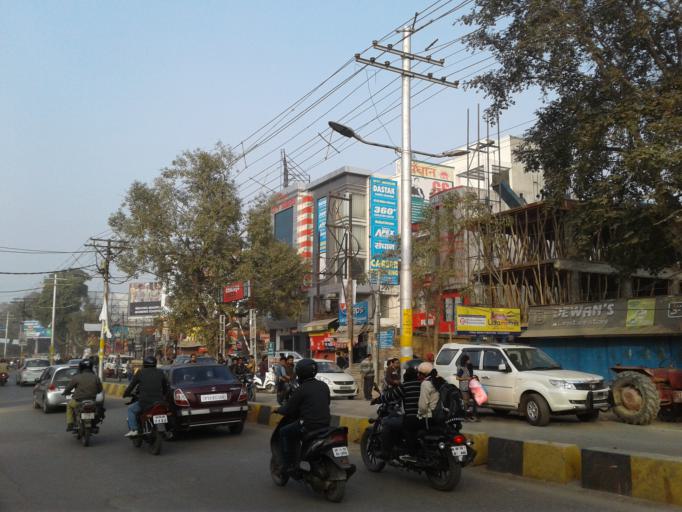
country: IN
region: Uttar Pradesh
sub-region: Allahabad
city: Allahabad
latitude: 25.4516
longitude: 81.8347
